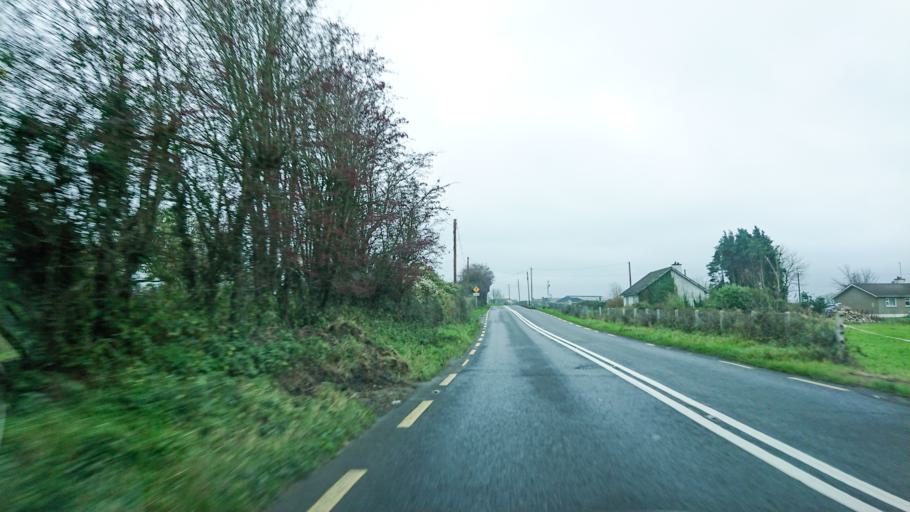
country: IE
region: Leinster
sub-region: Kilkenny
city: Mooncoin
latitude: 52.3053
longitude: -7.2790
